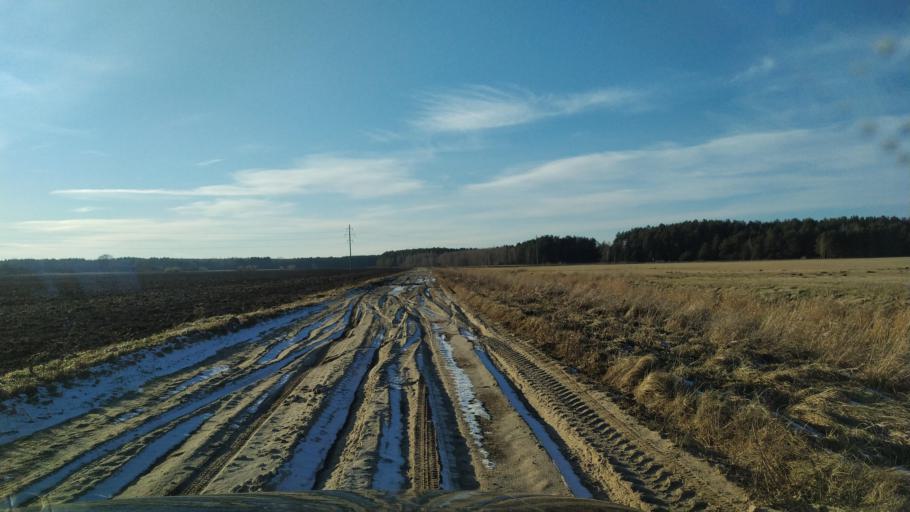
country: BY
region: Brest
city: Pruzhany
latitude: 52.5531
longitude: 24.3014
